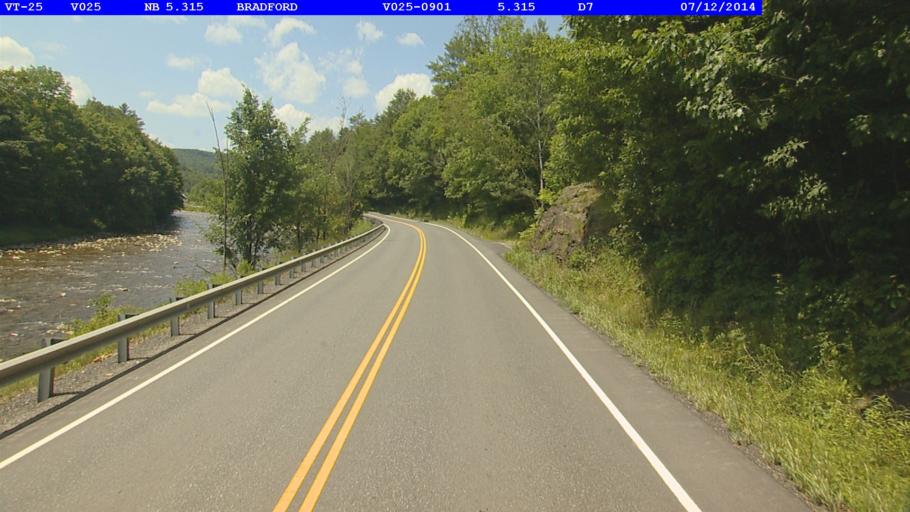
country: US
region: New Hampshire
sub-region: Grafton County
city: Haverhill
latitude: 44.0280
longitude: -72.1787
